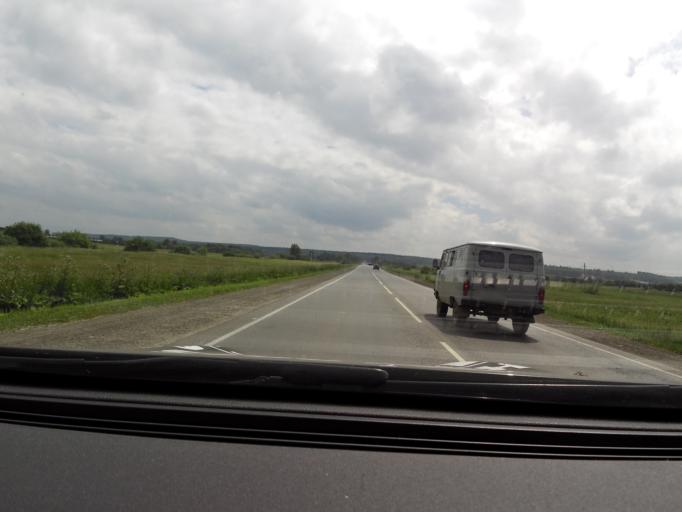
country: RU
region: Perm
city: Kukushtan
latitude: 57.5025
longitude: 56.6529
